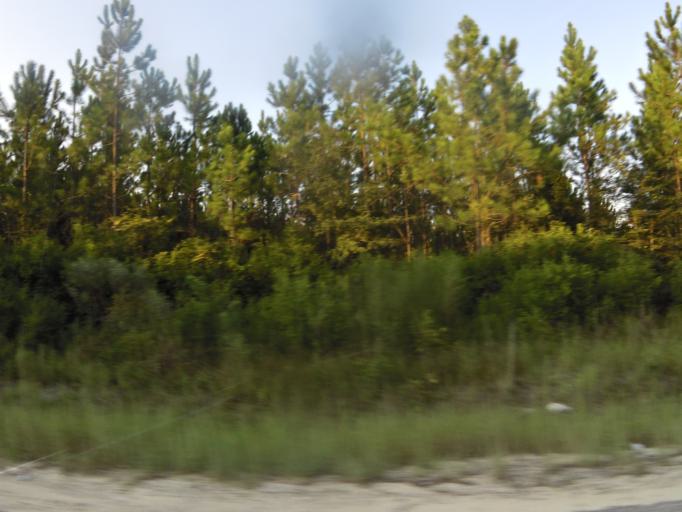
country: US
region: Florida
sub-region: Duval County
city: Baldwin
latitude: 30.3861
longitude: -82.0461
